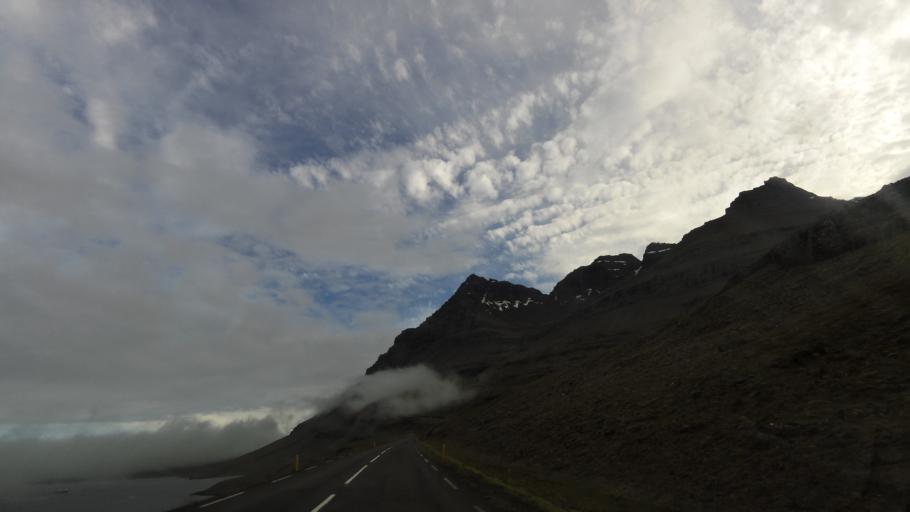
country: IS
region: East
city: Reydarfjoerdur
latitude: 64.7199
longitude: -14.4006
